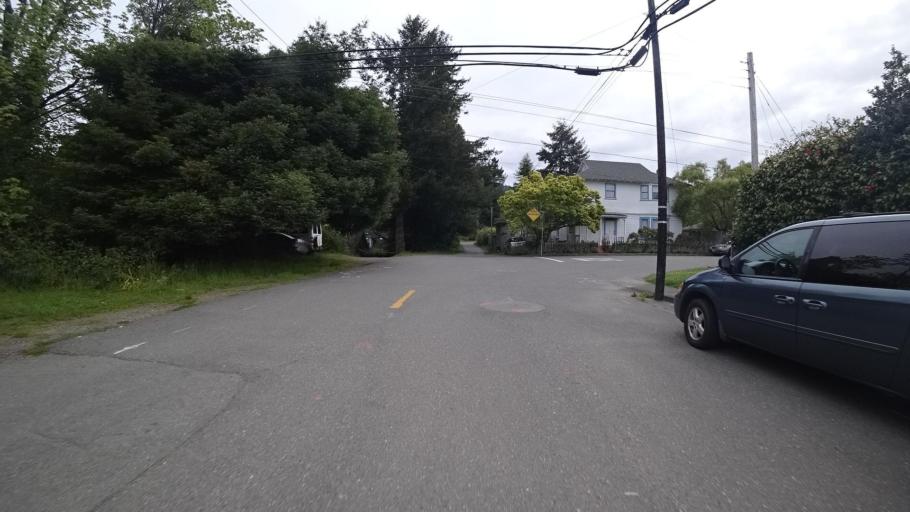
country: US
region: California
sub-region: Humboldt County
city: Blue Lake
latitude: 40.8819
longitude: -123.9872
